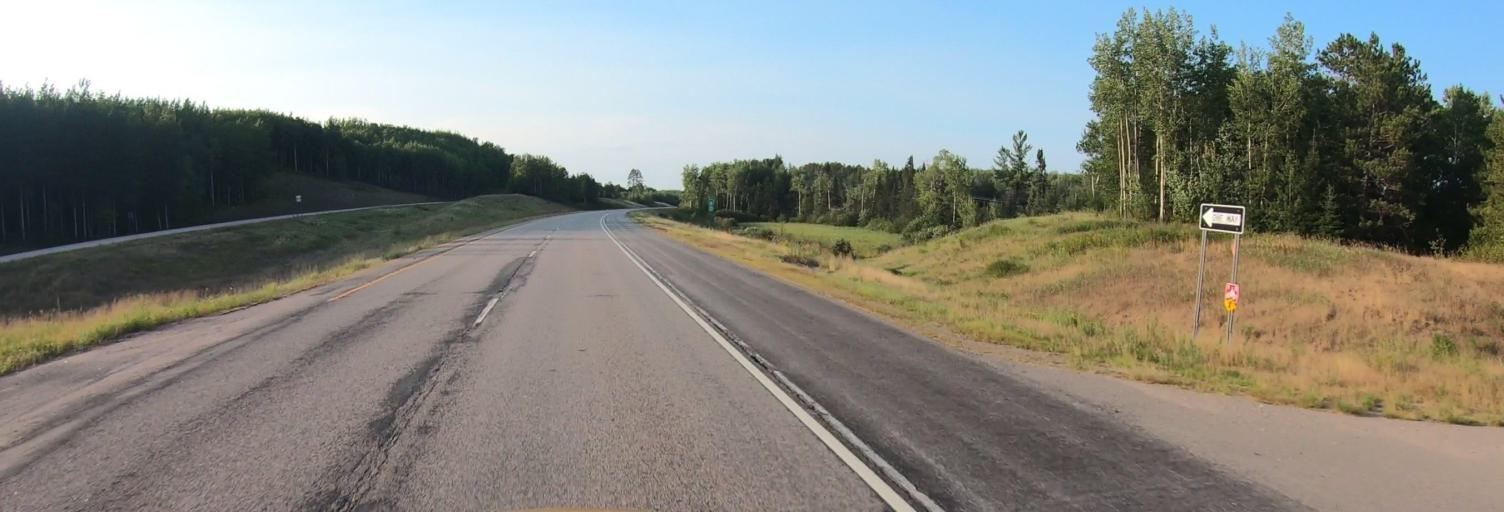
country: US
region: Minnesota
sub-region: Saint Louis County
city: Mountain Iron
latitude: 47.6810
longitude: -92.6376
